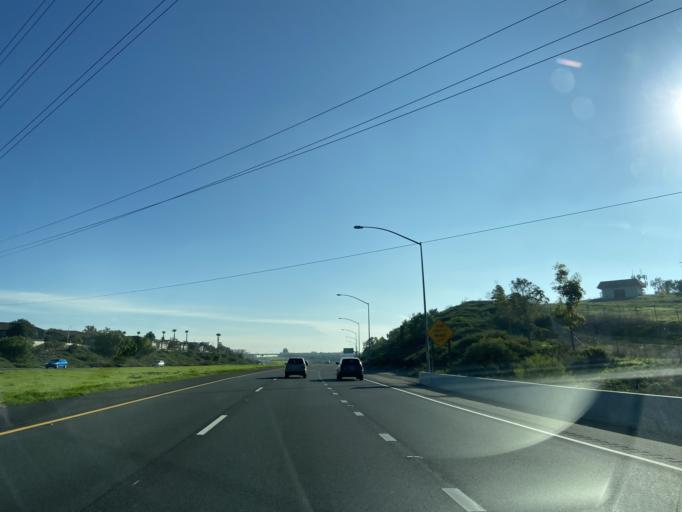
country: US
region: California
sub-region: San Diego County
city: Bonita
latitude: 32.6400
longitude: -116.9709
